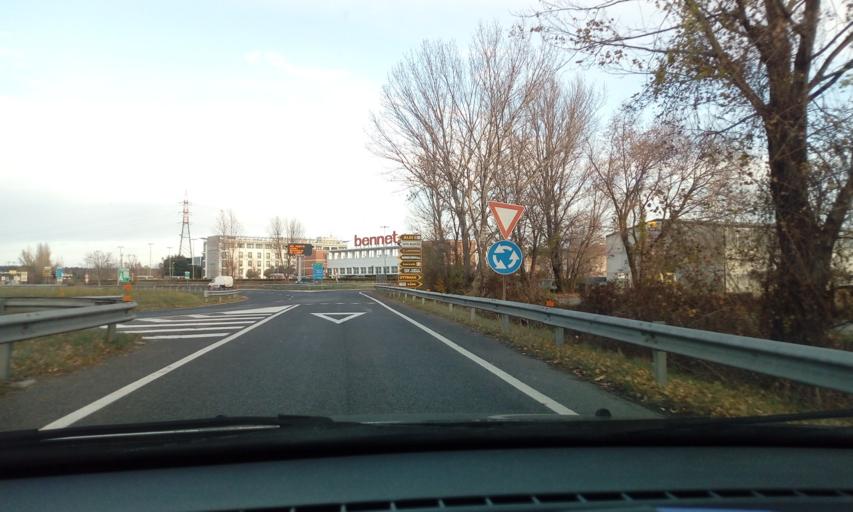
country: IT
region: Friuli Venezia Giulia
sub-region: Provincia di Gorizia
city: Ronchi dei Legionari
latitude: 45.8364
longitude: 13.4904
